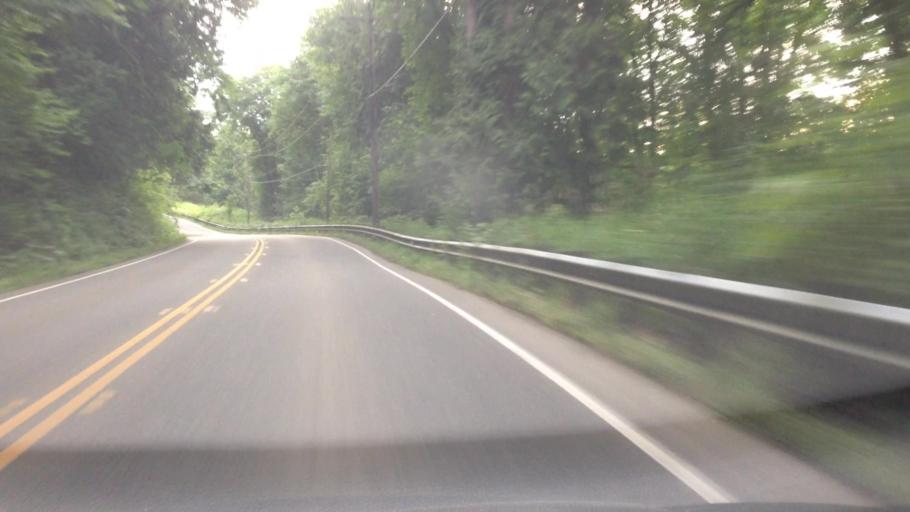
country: US
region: Washington
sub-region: King County
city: Duvall
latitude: 47.7508
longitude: -121.9725
